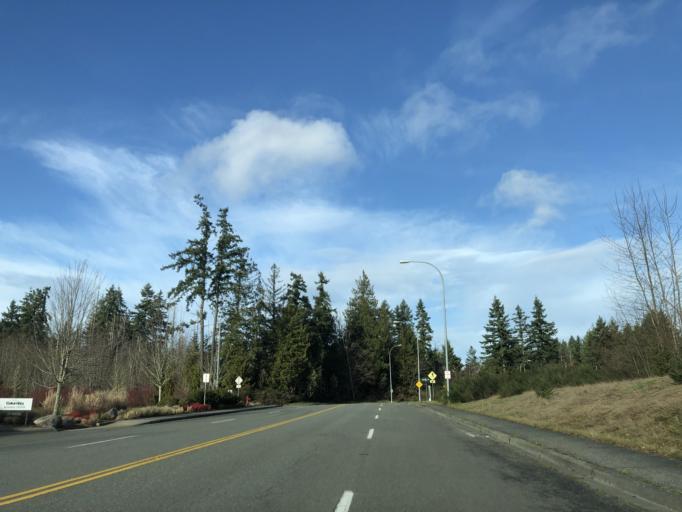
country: US
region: Washington
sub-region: Kitsap County
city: Poulsbo
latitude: 47.7644
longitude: -122.6555
